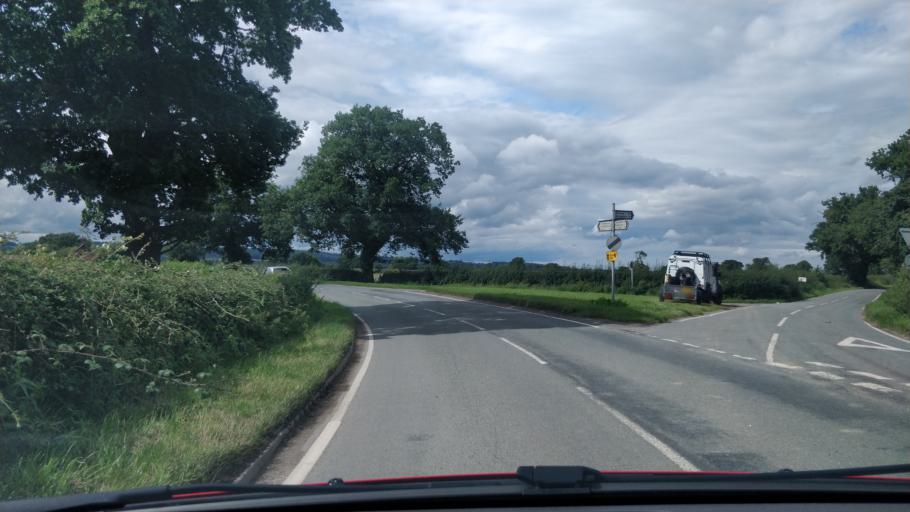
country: GB
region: Wales
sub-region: Wrexham
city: Rossett
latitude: 53.1526
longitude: -2.9632
